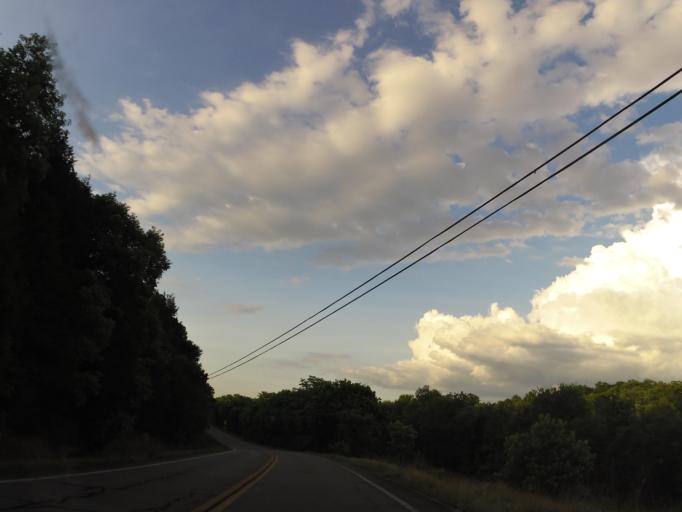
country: US
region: Georgia
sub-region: Dade County
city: Trenton
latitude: 34.9317
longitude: -85.4568
